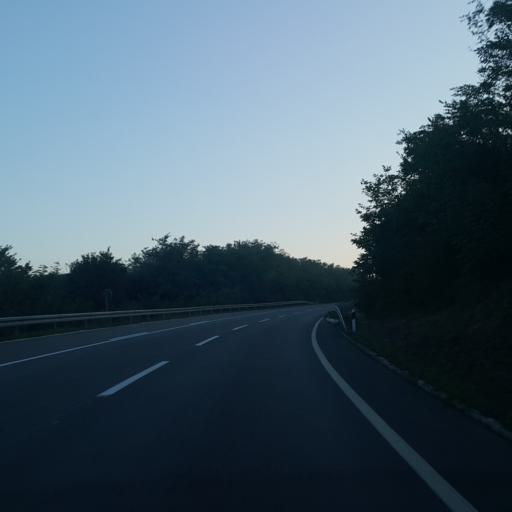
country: RS
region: Central Serbia
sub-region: Zajecarski Okrug
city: Zajecar
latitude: 43.9903
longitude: 22.2992
